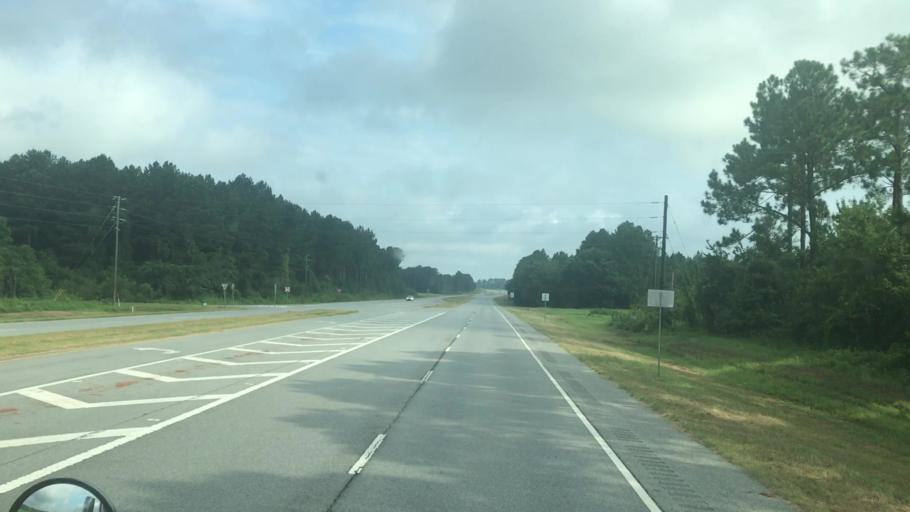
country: US
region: Georgia
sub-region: Miller County
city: Colquitt
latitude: 31.1956
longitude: -84.7672
